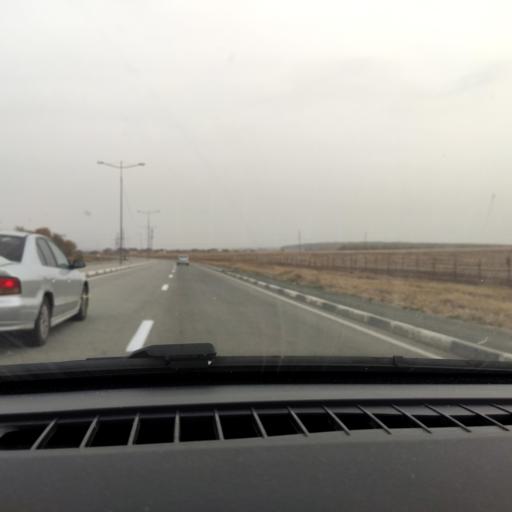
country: RU
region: Belgorod
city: Razumnoye
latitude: 50.5435
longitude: 36.7370
